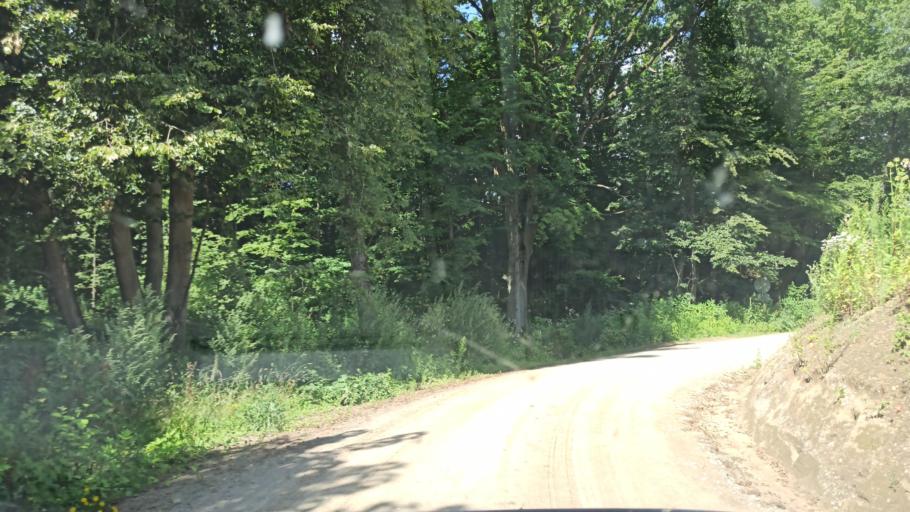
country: PL
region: Warmian-Masurian Voivodeship
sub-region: Powiat ostrodzki
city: Morag
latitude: 53.8574
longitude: 20.0654
